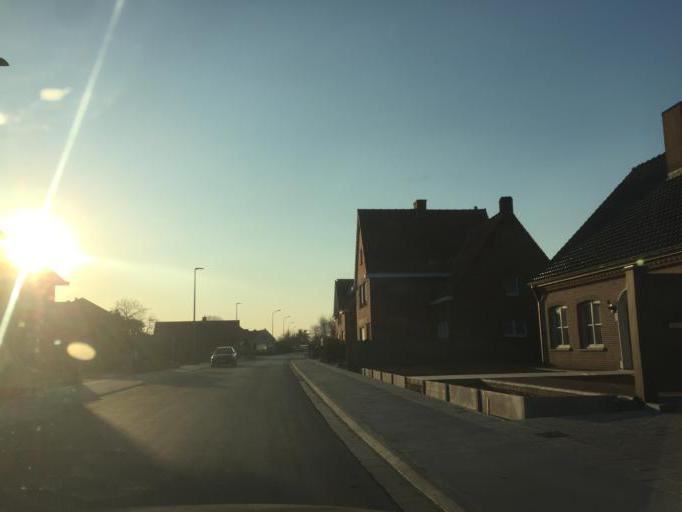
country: BE
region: Flanders
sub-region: Provincie West-Vlaanderen
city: Meulebeke
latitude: 50.9545
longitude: 3.3013
